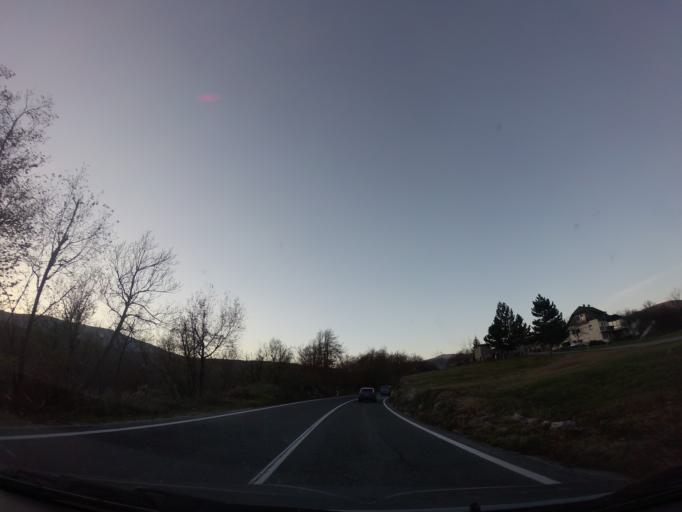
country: HR
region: Licko-Senjska
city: Jezerce
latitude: 44.9102
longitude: 15.6094
